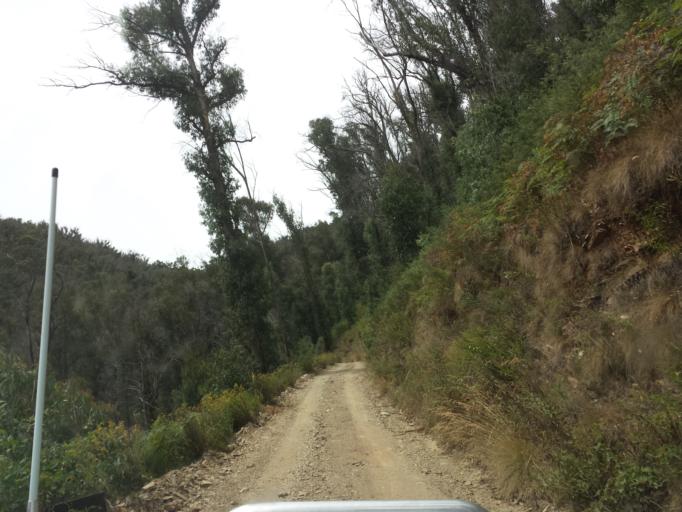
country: AU
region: Victoria
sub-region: Wellington
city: Heyfield
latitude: -37.7549
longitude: 146.5182
